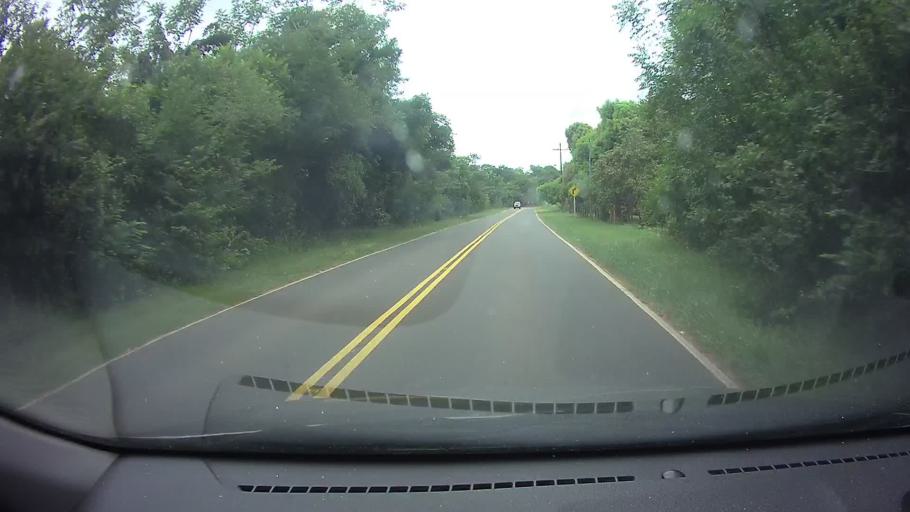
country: PY
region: Central
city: Nueva Italia
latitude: -25.6118
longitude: -57.4331
